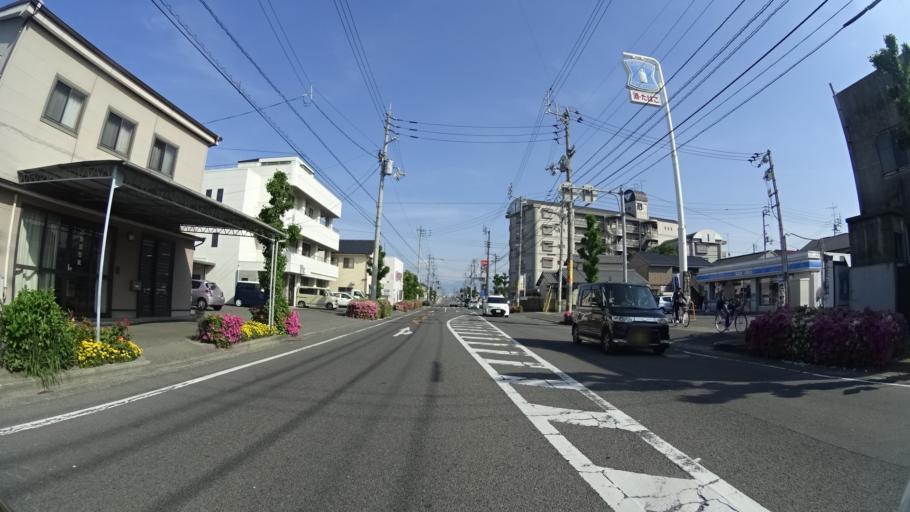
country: JP
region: Ehime
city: Saijo
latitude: 34.0614
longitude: 133.0109
